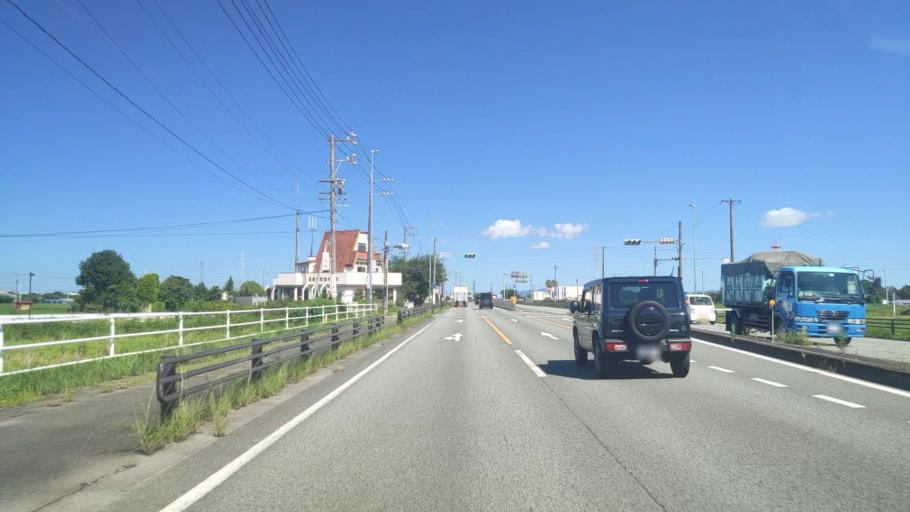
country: JP
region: Mie
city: Hisai-motomachi
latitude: 34.5972
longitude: 136.5385
